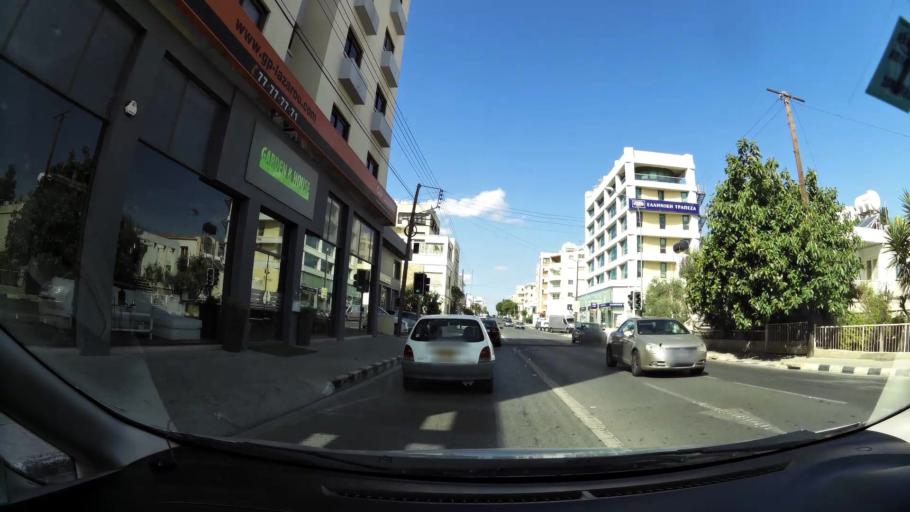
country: CY
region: Lefkosia
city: Nicosia
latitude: 35.1411
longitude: 33.3718
